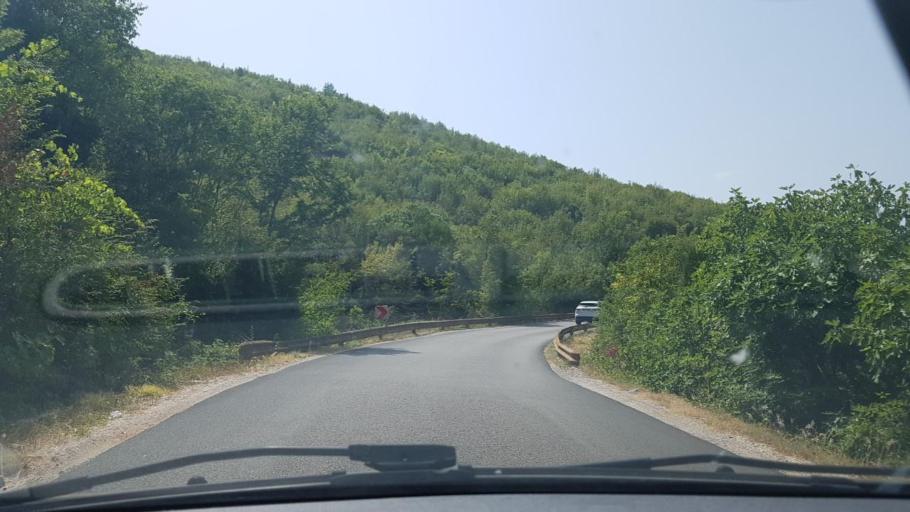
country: HR
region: Dubrovacko-Neretvanska
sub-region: Grad Dubrovnik
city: Metkovic
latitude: 43.0378
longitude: 17.7174
